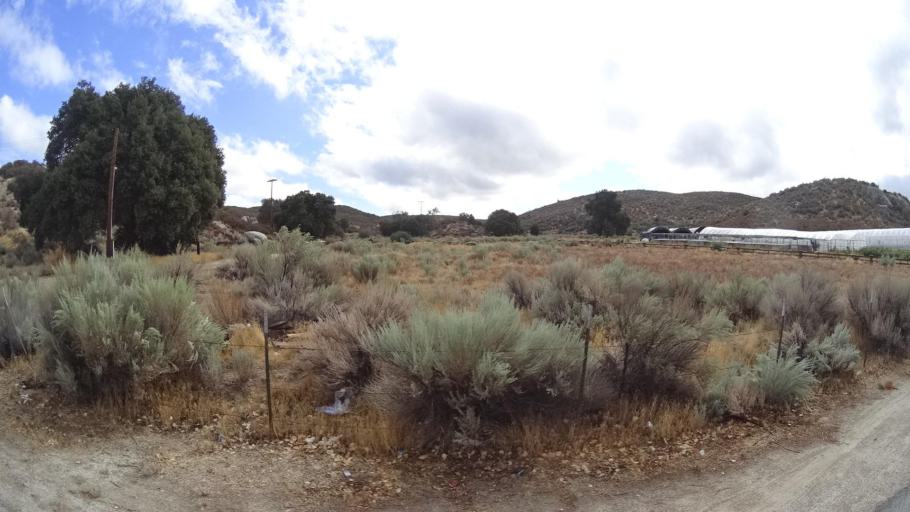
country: US
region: California
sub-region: San Diego County
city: Campo
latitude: 32.7232
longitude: -116.4271
